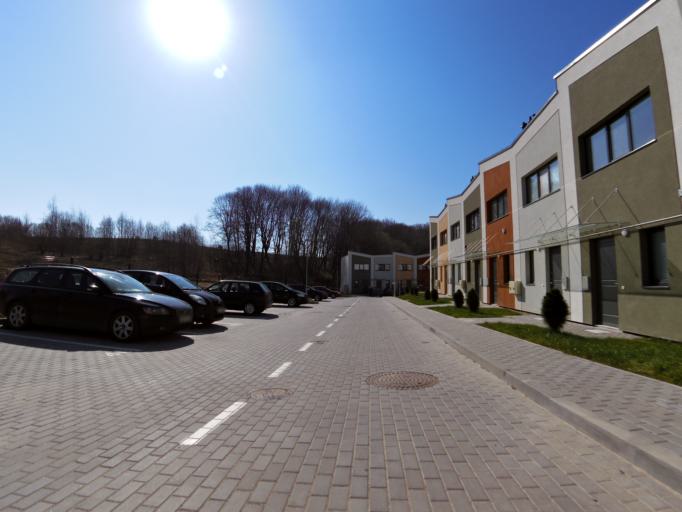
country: LT
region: Vilnius County
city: Justiniskes
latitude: 54.7189
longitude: 25.2034
